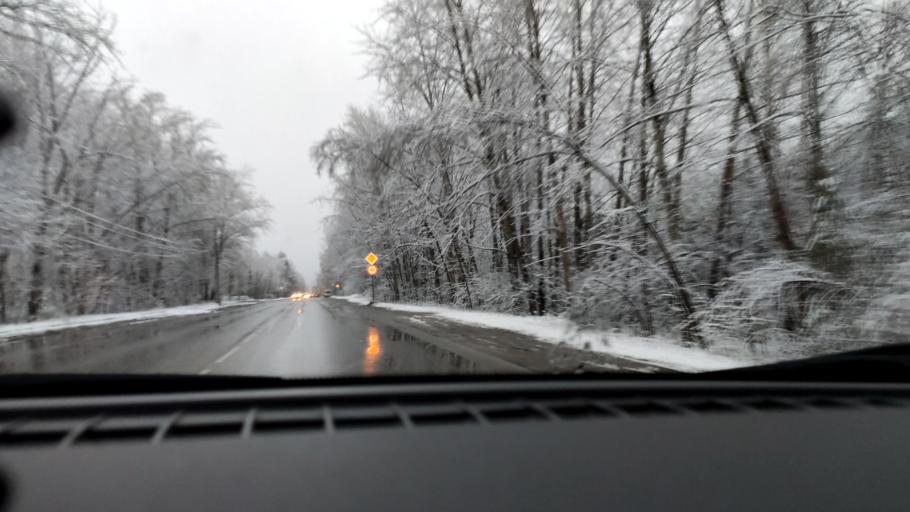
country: RU
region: Perm
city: Overyata
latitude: 58.0149
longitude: 55.9028
